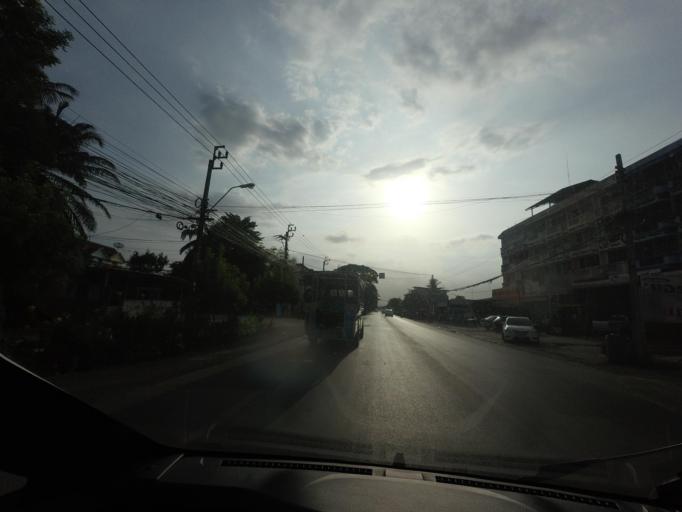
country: TH
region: Bangkok
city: Nong Chok
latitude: 13.8522
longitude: 100.8760
